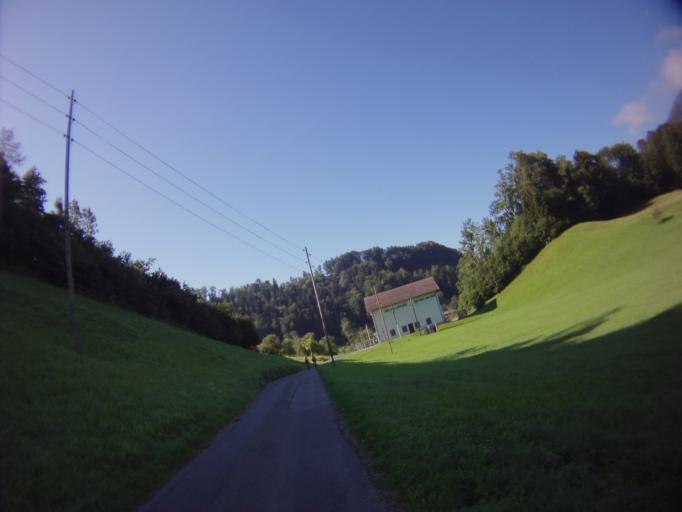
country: CH
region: Schwyz
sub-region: Bezirk Schwyz
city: Sattel
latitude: 47.0987
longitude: 8.6426
